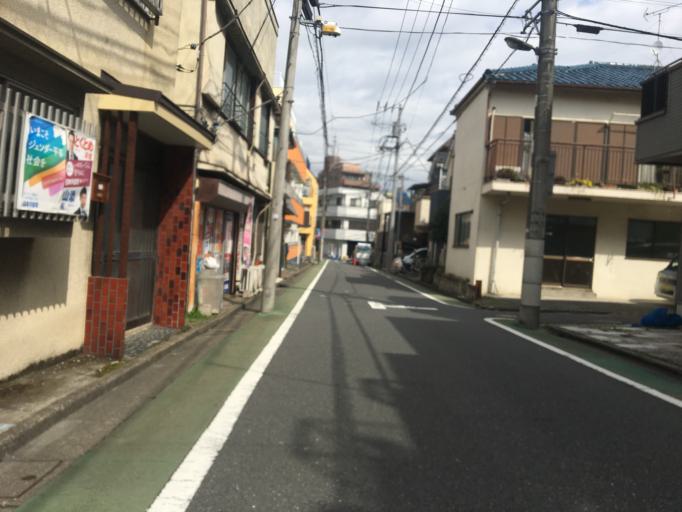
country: JP
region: Tokyo
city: Tokyo
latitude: 35.7481
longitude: 139.6807
